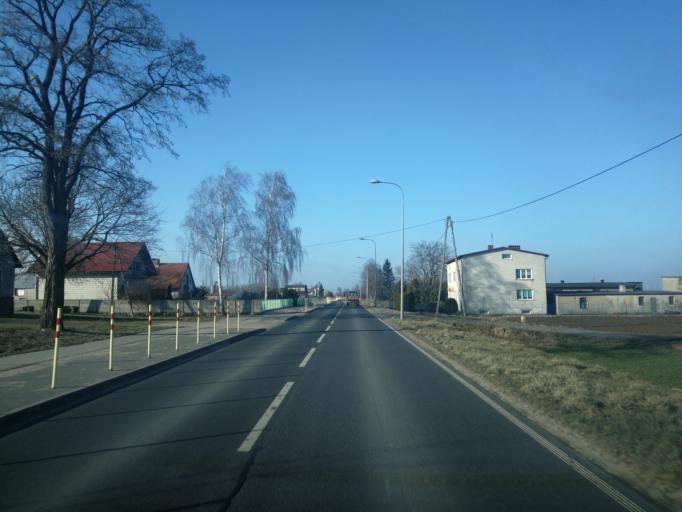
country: PL
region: Warmian-Masurian Voivodeship
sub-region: Powiat ilawski
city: Lubawa
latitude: 53.4674
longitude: 19.7714
